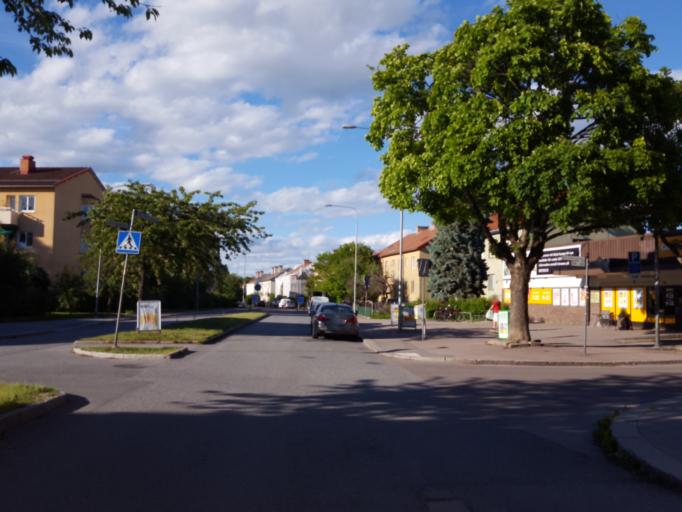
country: SE
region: Uppsala
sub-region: Uppsala Kommun
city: Uppsala
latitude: 59.8586
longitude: 17.6565
